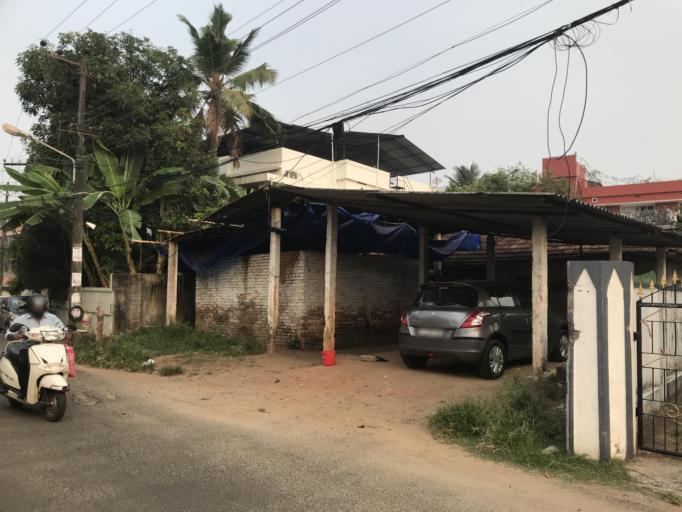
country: IN
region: Kerala
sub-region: Ernakulam
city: Elur
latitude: 10.0041
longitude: 76.2909
